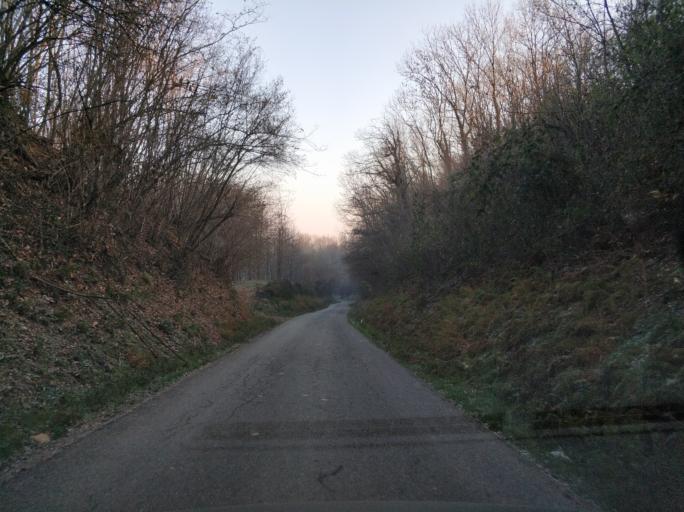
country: IT
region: Piedmont
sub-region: Provincia di Torino
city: Barbania
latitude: 45.2951
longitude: 7.6307
